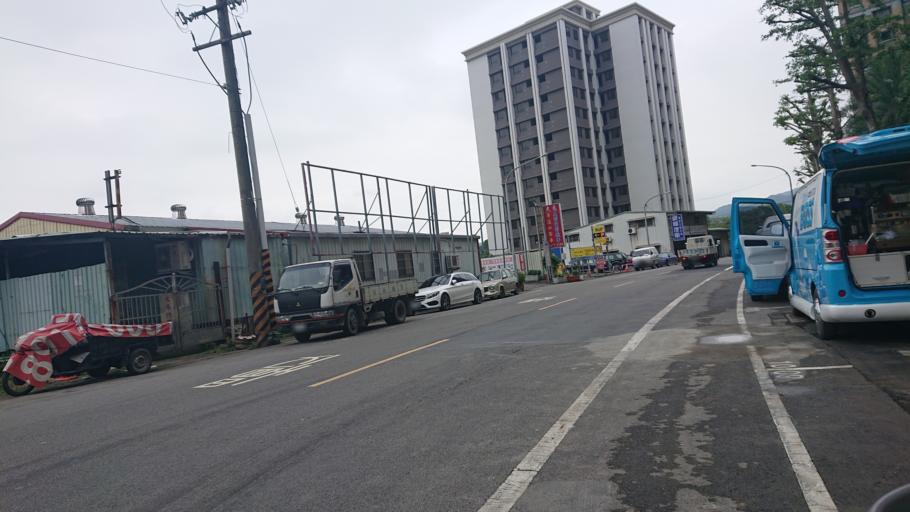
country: TW
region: Taiwan
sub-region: Taoyuan
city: Taoyuan
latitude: 24.9368
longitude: 121.3606
